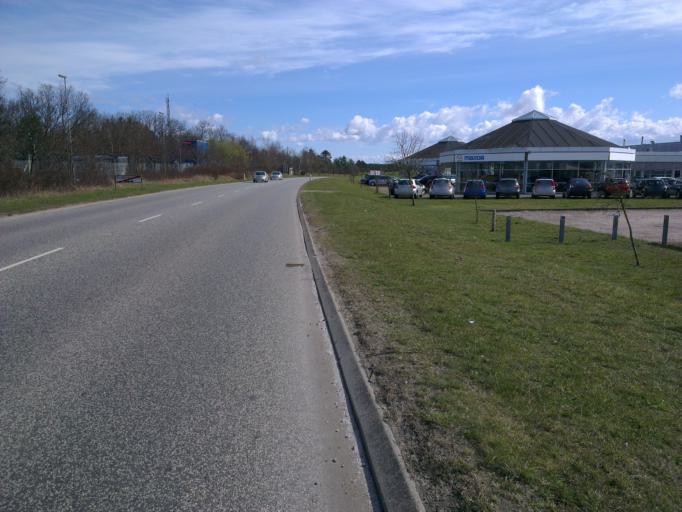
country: DK
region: Capital Region
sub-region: Frederikssund Kommune
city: Frederikssund
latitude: 55.8253
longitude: 12.0928
